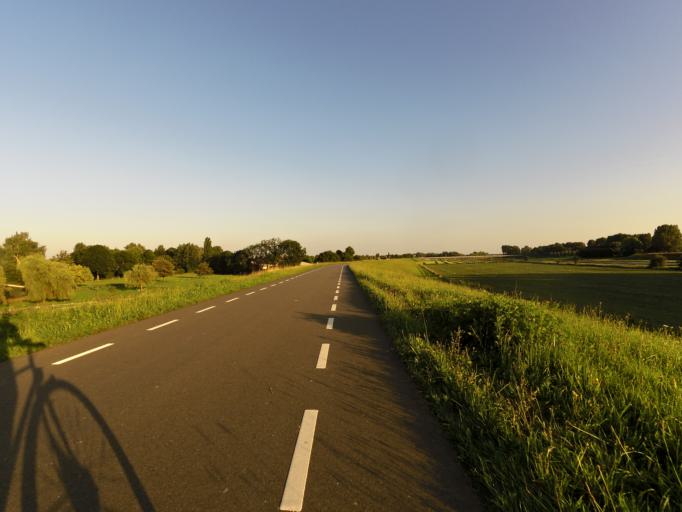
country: NL
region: Gelderland
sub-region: Gemeente Duiven
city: Duiven
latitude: 51.8970
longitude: 6.0271
